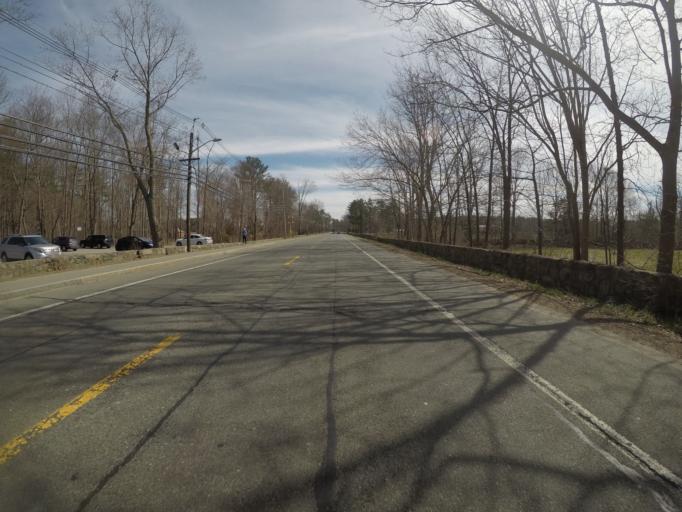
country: US
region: Massachusetts
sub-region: Bristol County
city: Easton
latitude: 42.0613
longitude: -71.0869
